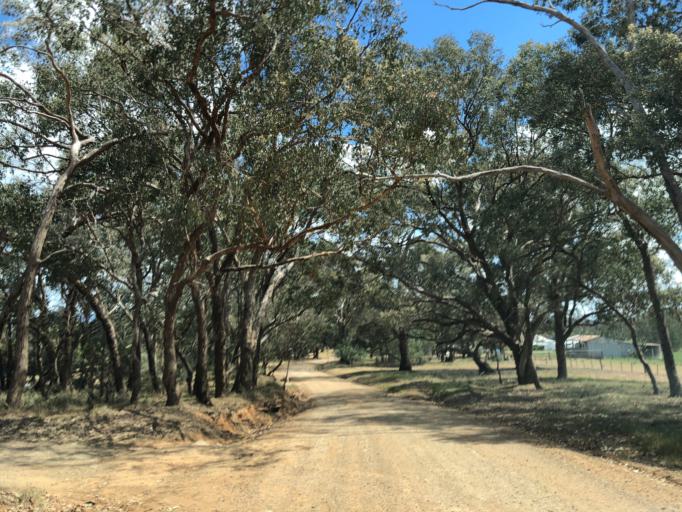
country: AU
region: Victoria
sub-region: Benalla
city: Benalla
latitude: -36.7292
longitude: 146.1189
